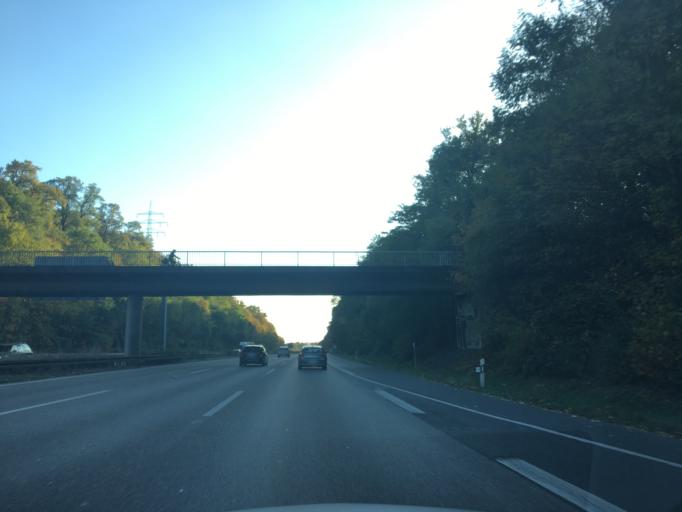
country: DE
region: Hesse
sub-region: Regierungsbezirk Darmstadt
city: Offenbach
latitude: 50.0930
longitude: 8.7399
